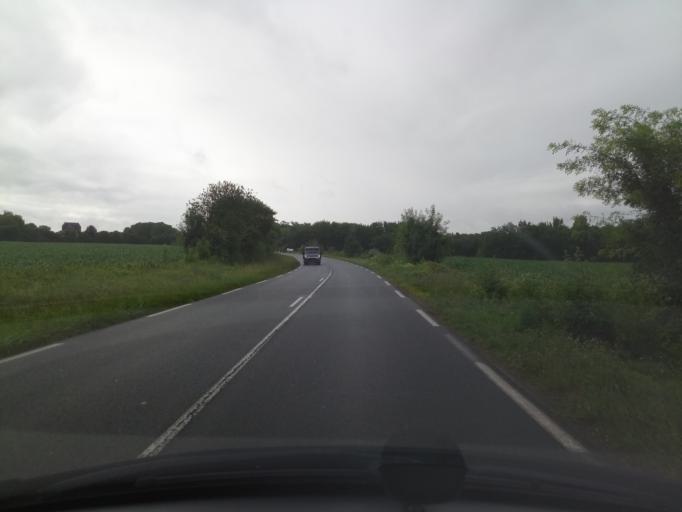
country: FR
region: Poitou-Charentes
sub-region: Departement de la Charente-Maritime
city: Courcon
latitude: 46.1662
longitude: -0.8350
